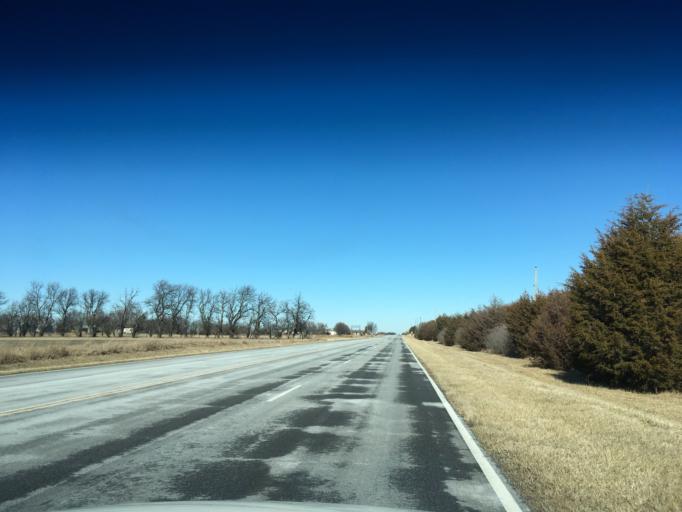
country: US
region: Kansas
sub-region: Harvey County
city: Sedgwick
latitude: 37.9515
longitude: -97.3364
